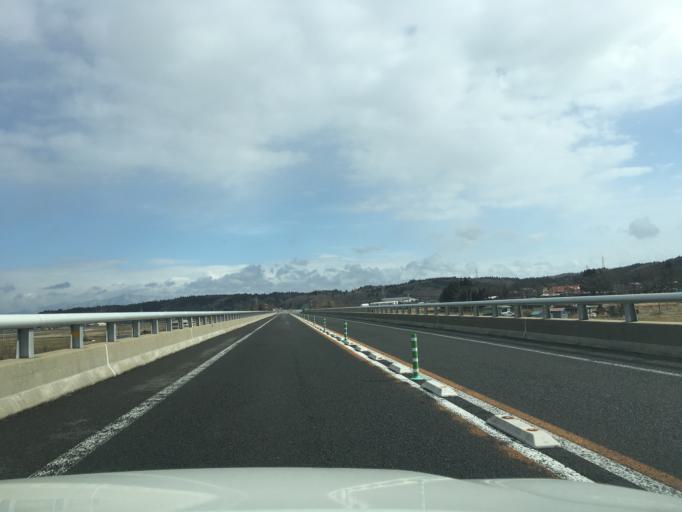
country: JP
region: Akita
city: Akita
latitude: 39.6211
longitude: 140.1512
